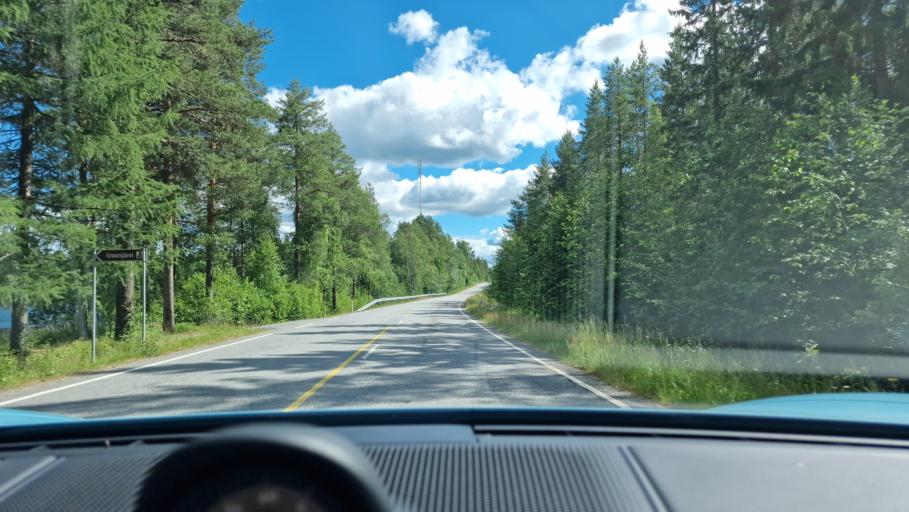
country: FI
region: Southern Ostrobothnia
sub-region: Jaerviseutu
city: Soini
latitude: 62.8233
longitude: 24.3444
